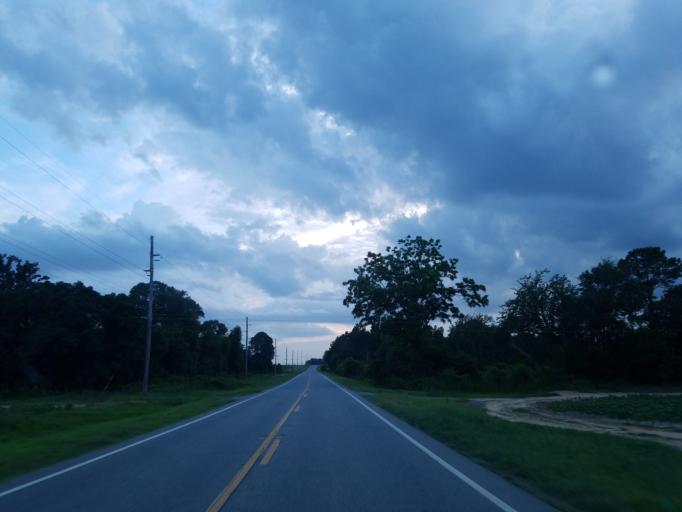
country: US
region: Georgia
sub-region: Dooly County
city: Vienna
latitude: 32.1238
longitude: -83.7318
